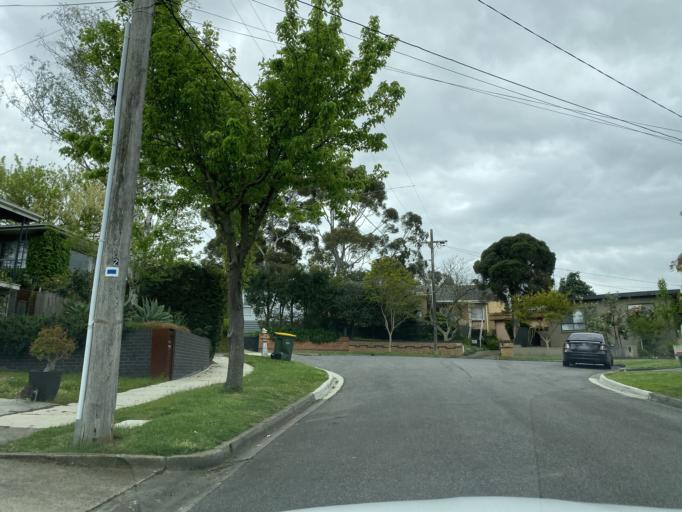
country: AU
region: Victoria
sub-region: Whitehorse
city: Box Hill South
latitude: -37.8345
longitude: 145.1174
